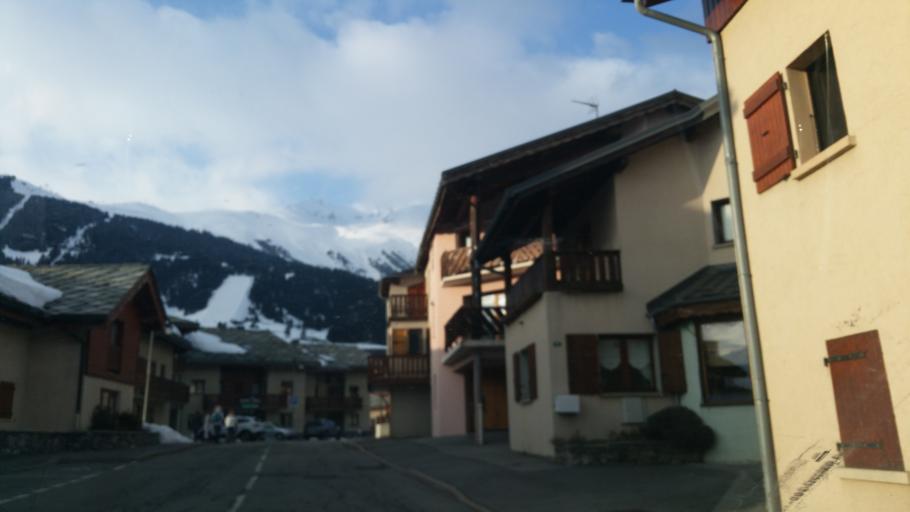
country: FR
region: Rhone-Alpes
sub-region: Departement de la Savoie
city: Modane
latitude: 45.2276
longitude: 6.7449
